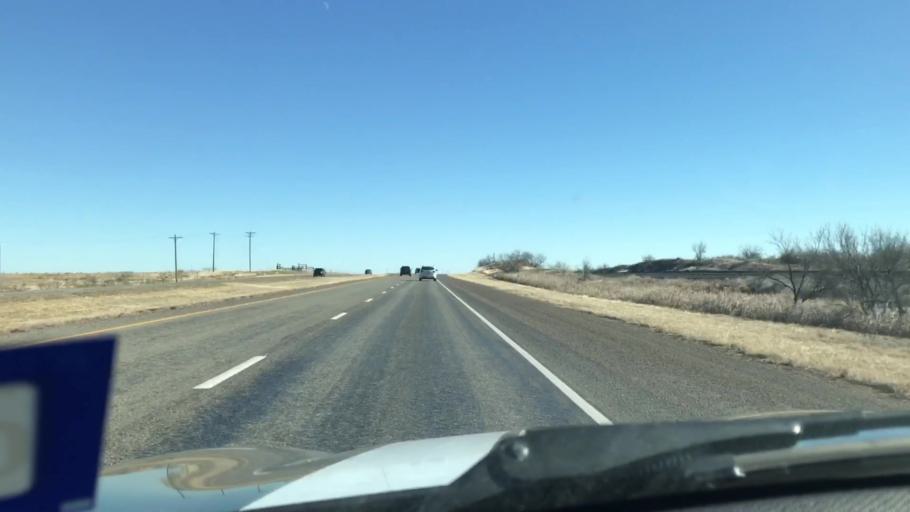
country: US
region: Texas
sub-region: Garza County
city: Post
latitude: 33.1394
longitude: -101.3155
